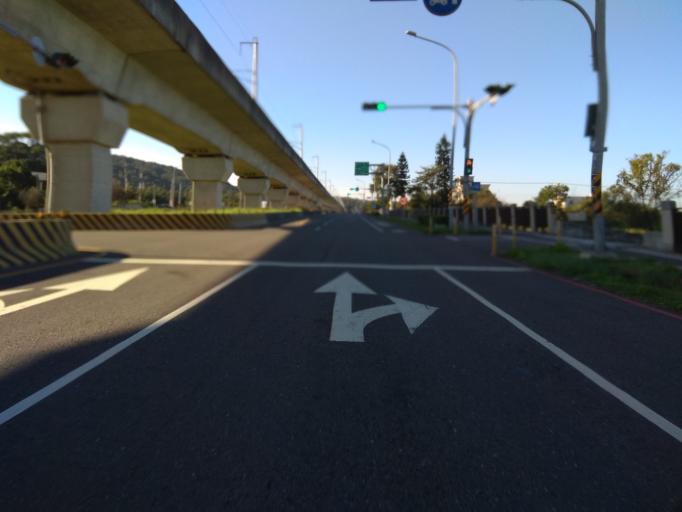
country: TW
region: Taiwan
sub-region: Hsinchu
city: Zhubei
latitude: 24.8865
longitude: 121.0722
